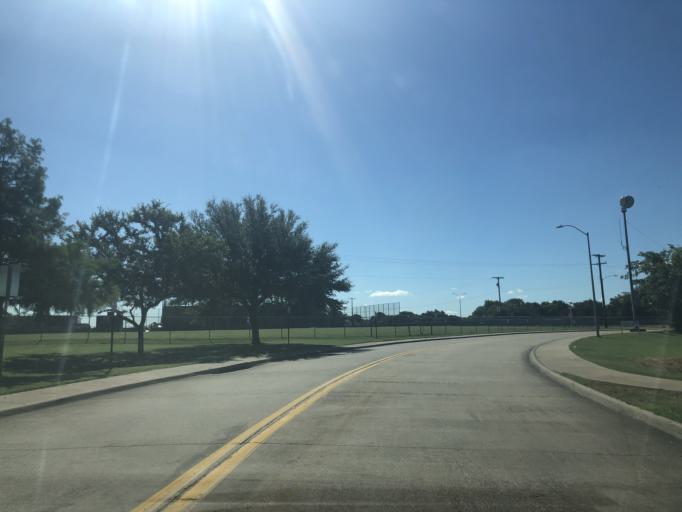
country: US
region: Texas
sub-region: Dallas County
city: Duncanville
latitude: 32.6594
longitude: -96.9327
